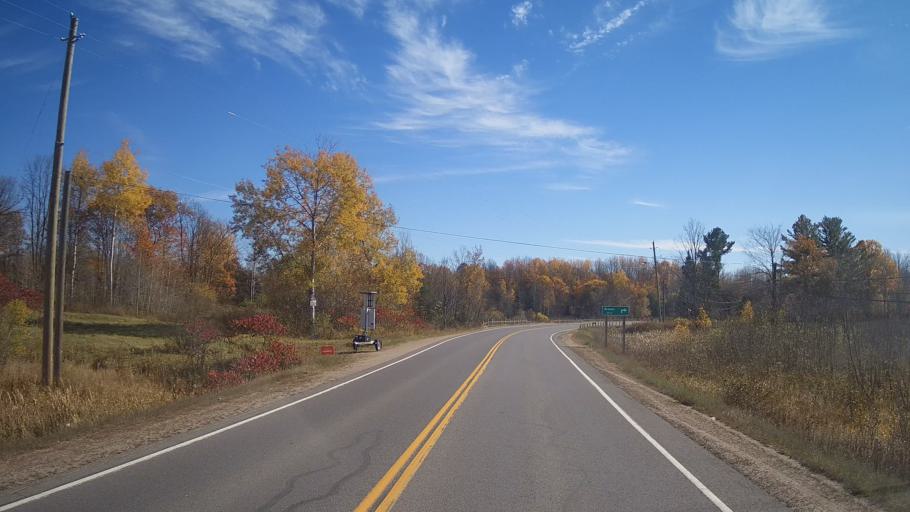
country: CA
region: Ontario
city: Perth
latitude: 44.7629
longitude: -76.6863
